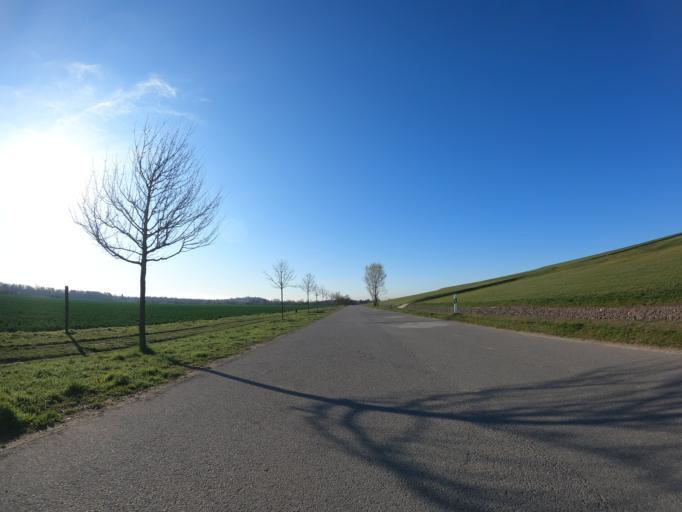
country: DE
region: Berlin
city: Gropiusstadt
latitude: 52.4124
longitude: 13.4635
